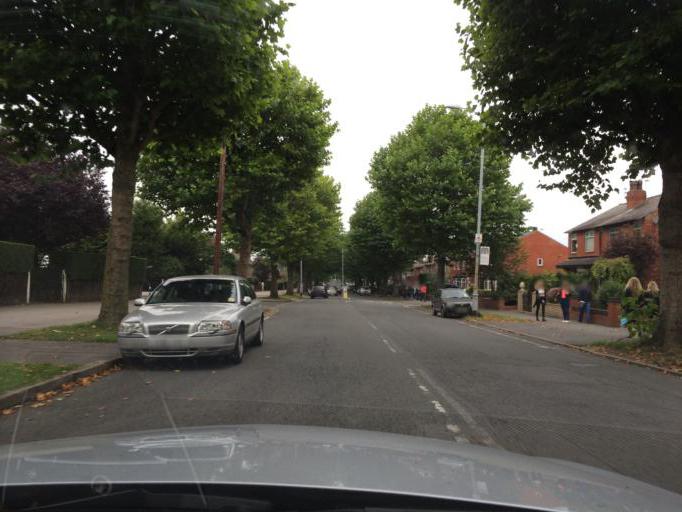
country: GB
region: England
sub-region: Borough of Stockport
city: Hazel Grove
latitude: 53.3972
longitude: -2.1350
